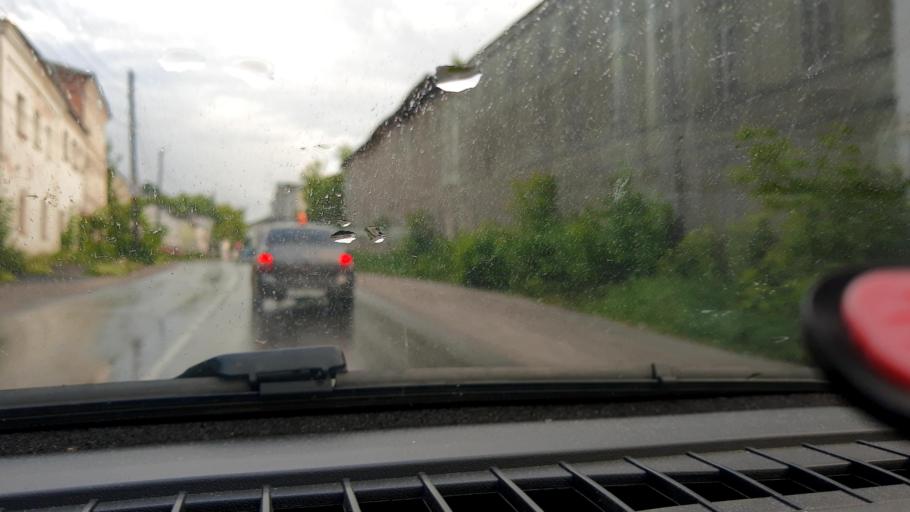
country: RU
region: Nizjnij Novgorod
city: Gorodets
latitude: 56.6468
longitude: 43.4646
